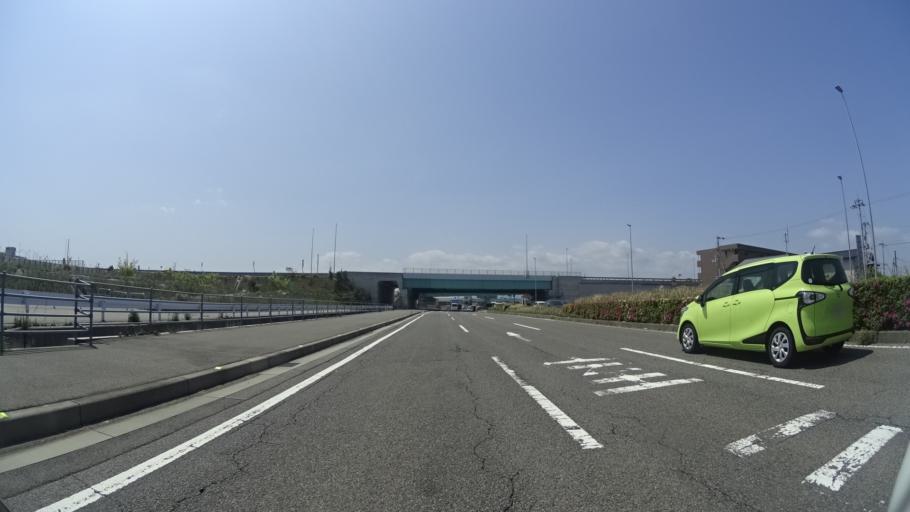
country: JP
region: Tokushima
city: Tokushima-shi
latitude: 34.1024
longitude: 134.5756
